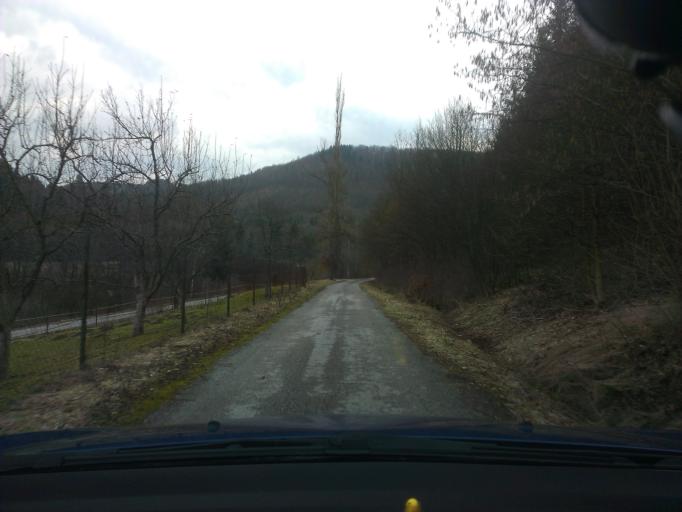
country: SK
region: Banskobystricky
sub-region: Okres Banska Bystrica
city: Banska Stiavnica
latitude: 48.4569
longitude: 18.9353
